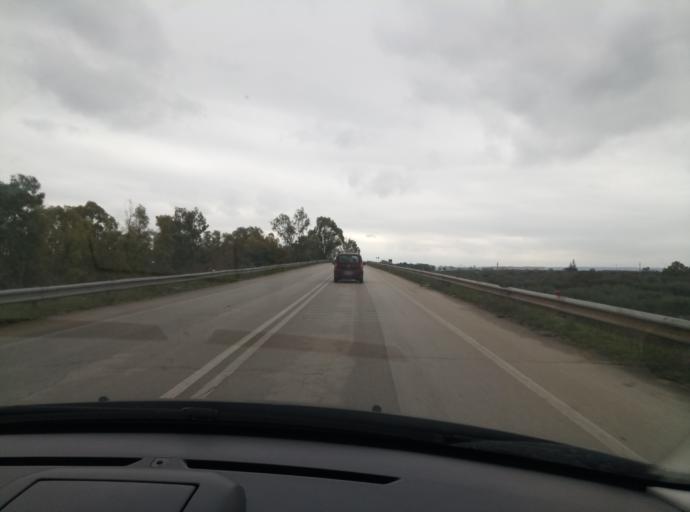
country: IT
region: Apulia
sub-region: Provincia di Bari
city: Acquaviva delle Fonti
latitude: 40.9229
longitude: 16.8575
